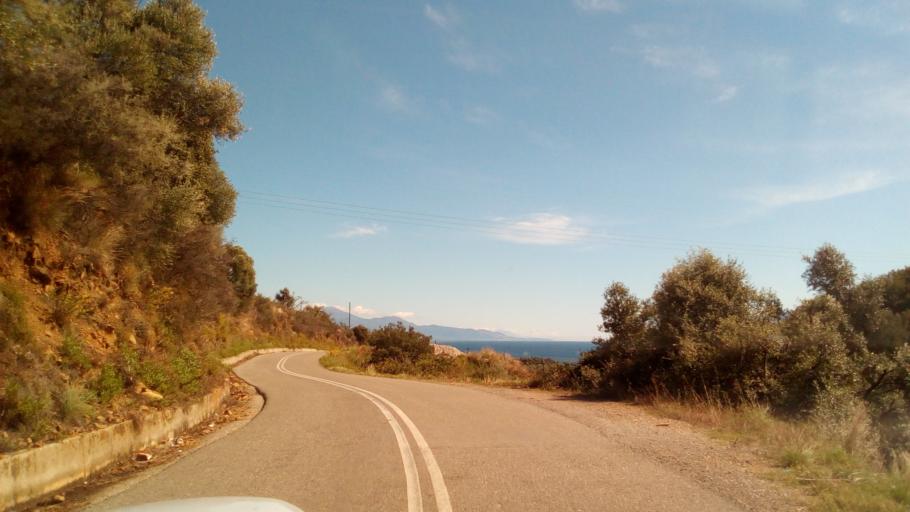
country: GR
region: West Greece
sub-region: Nomos Aitolias kai Akarnanias
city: Antirrio
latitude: 38.3688
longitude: 21.7708
